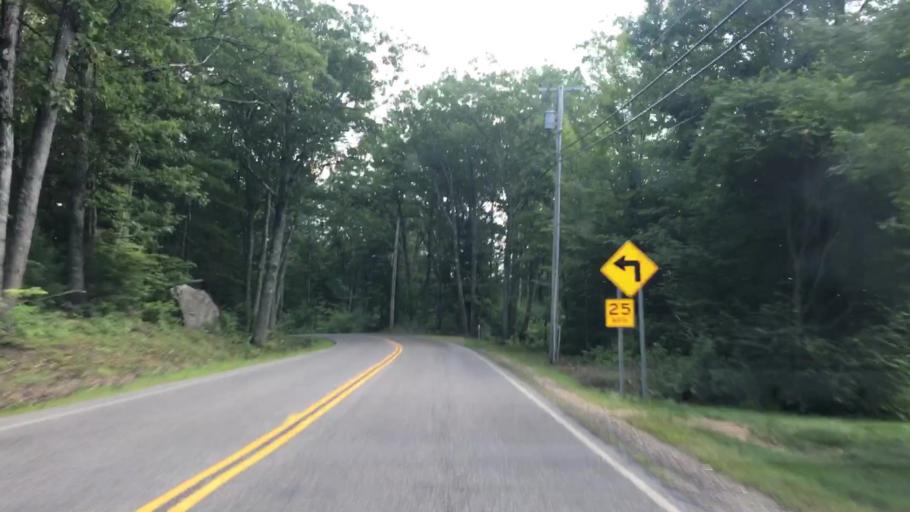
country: US
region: New Hampshire
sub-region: Belknap County
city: Sanbornton
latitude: 43.4946
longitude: -71.5905
